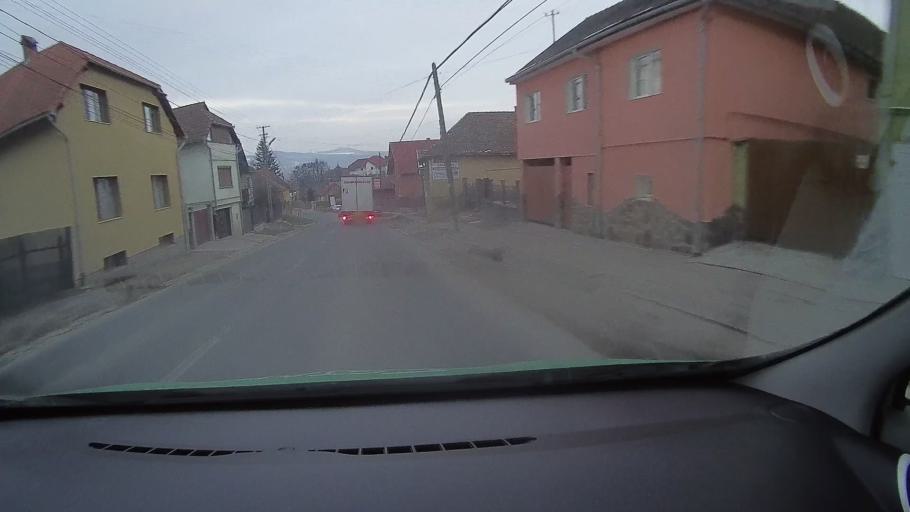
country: RO
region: Harghita
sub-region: Municipiul Odorheiu Secuiesc
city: Odorheiu Secuiesc
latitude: 46.3159
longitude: 25.2824
